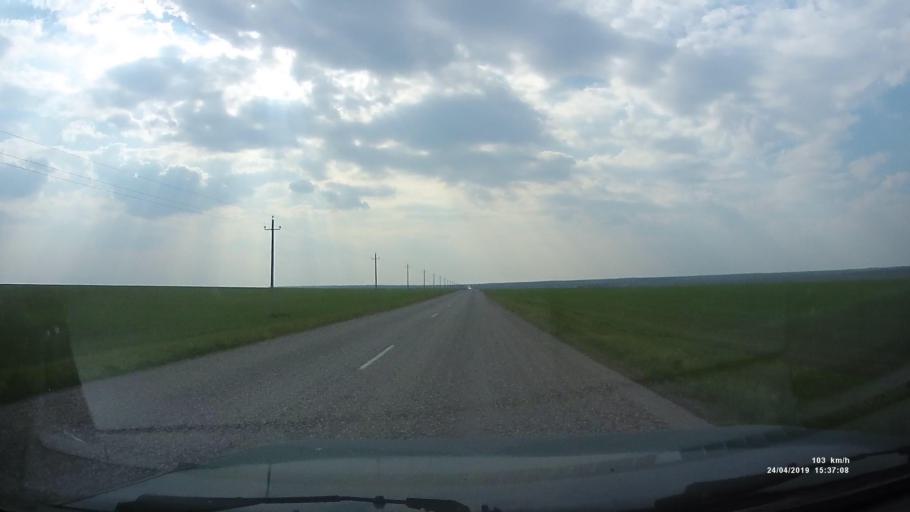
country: RU
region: Kalmykiya
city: Yashalta
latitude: 46.5994
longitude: 42.8555
